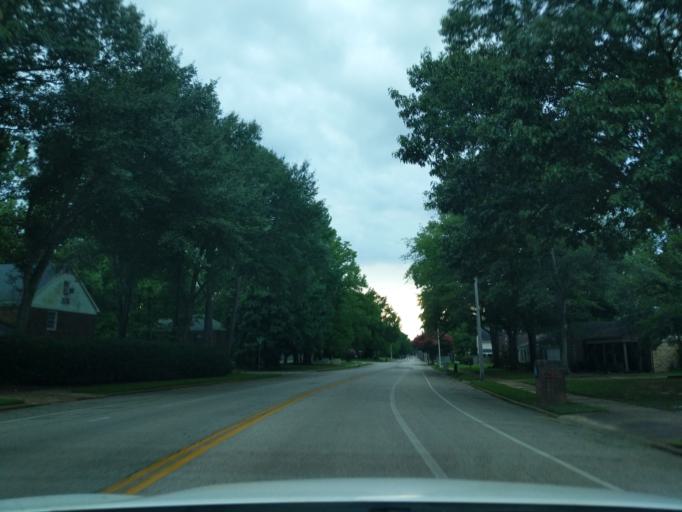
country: US
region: Tennessee
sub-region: Shelby County
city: Germantown
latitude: 35.0768
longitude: -89.8332
